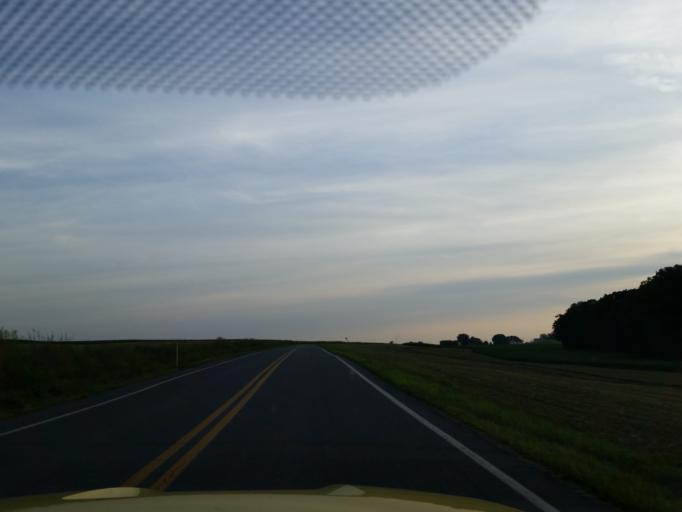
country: US
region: Pennsylvania
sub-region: Lebanon County
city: Fredericksburg
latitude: 40.4345
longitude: -76.3958
